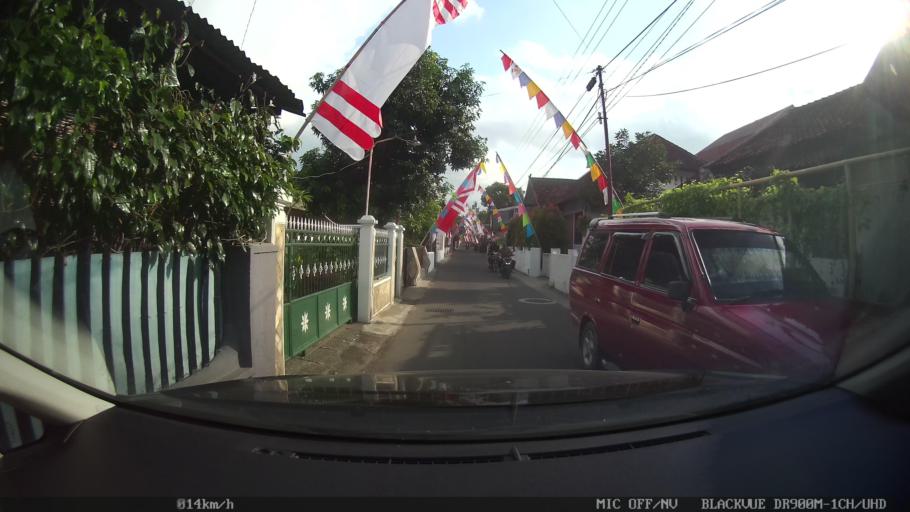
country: ID
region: Daerah Istimewa Yogyakarta
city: Kasihan
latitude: -7.8165
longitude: 110.3590
